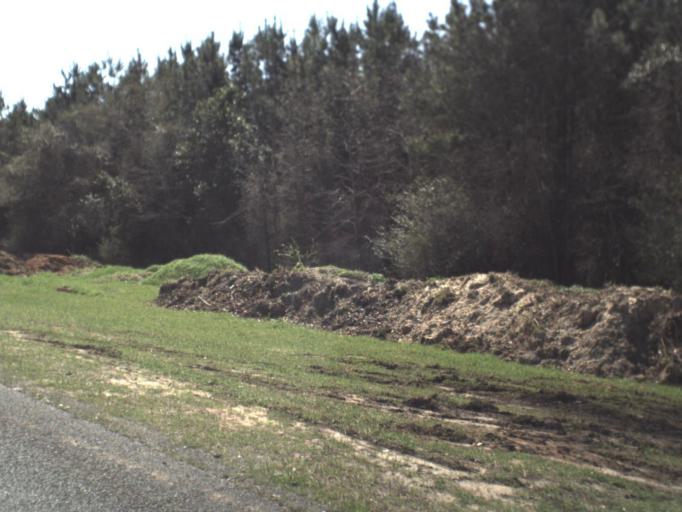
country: US
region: Florida
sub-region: Jackson County
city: Graceville
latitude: 30.9568
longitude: -85.4028
